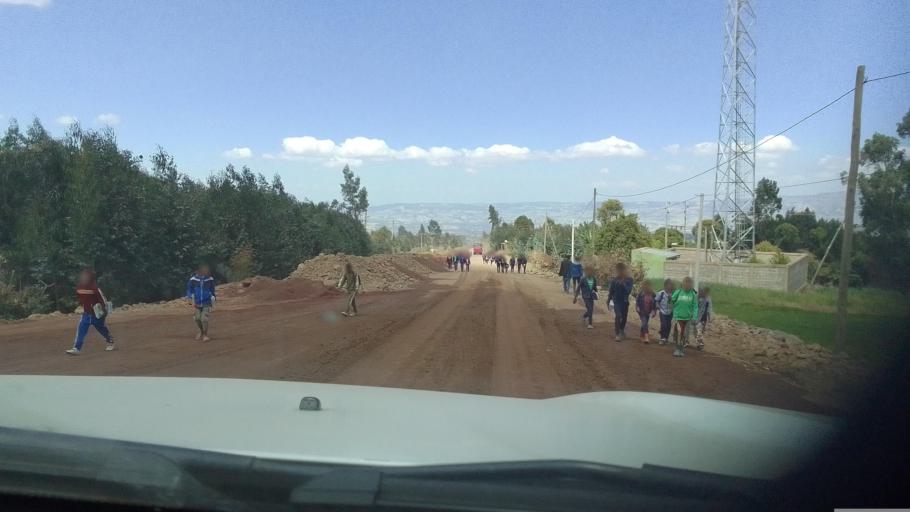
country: ET
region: Oromiya
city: Hagere Hiywet
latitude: 8.8547
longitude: 37.8929
